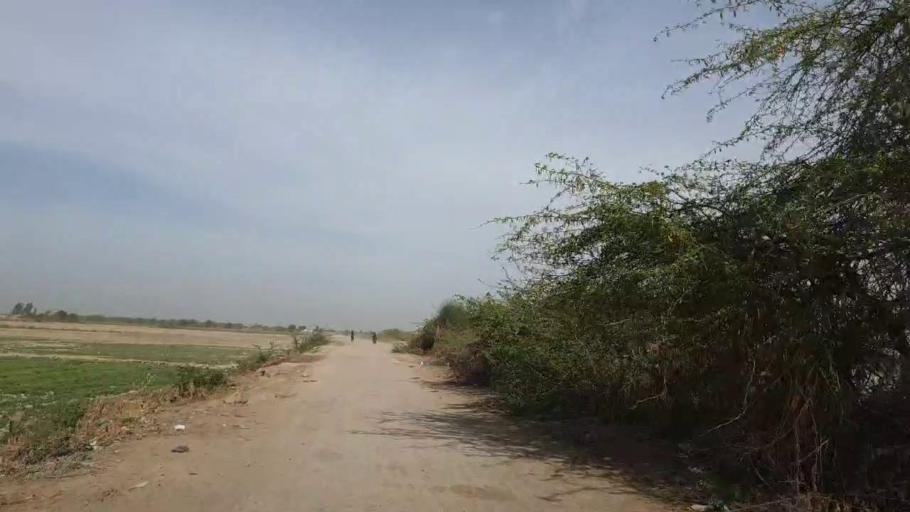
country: PK
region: Sindh
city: Kunri
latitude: 25.1700
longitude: 69.6175
